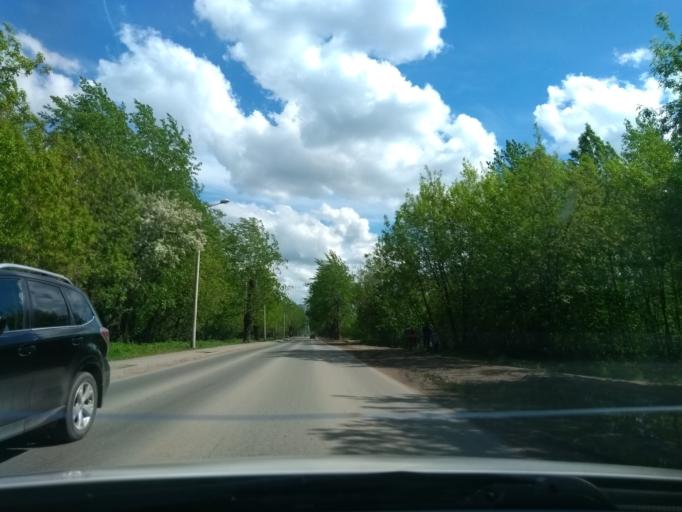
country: RU
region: Perm
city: Kondratovo
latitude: 58.0047
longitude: 56.1258
